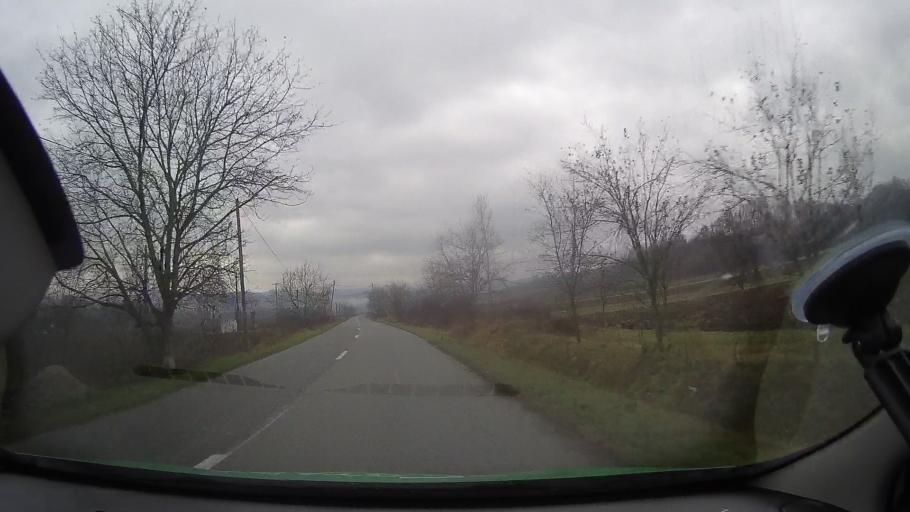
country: RO
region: Arad
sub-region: Comuna Gurahont
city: Gurahont
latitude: 46.2563
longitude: 22.3349
